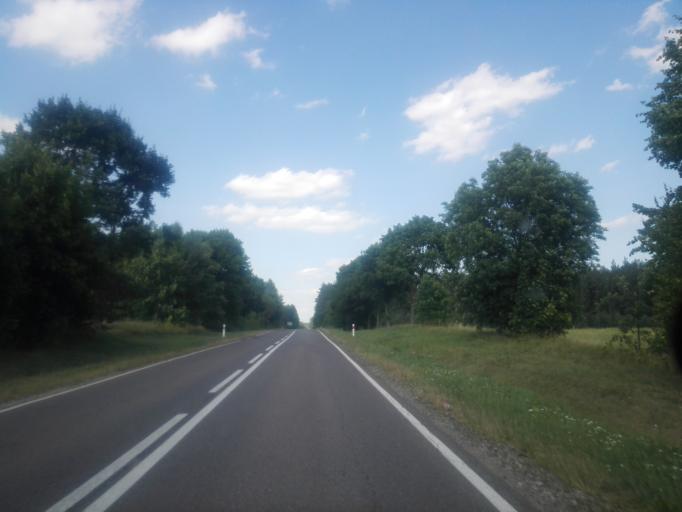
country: PL
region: Podlasie
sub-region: Powiat sejnenski
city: Sejny
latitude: 54.0278
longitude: 23.3475
